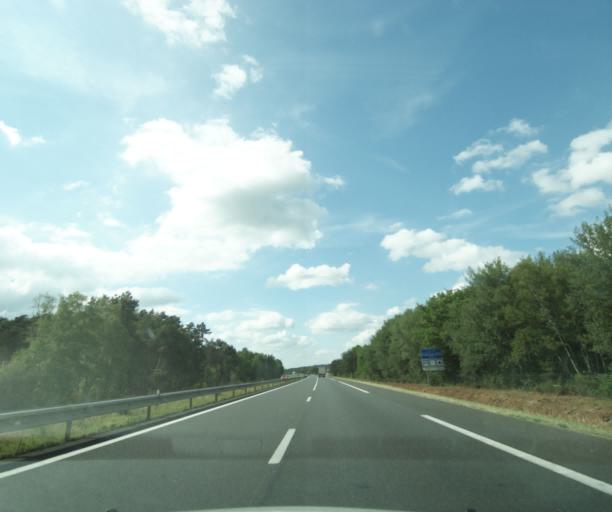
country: FR
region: Centre
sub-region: Departement du Loir-et-Cher
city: Chaumont-sur-Tharonne
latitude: 47.6588
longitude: 1.9326
